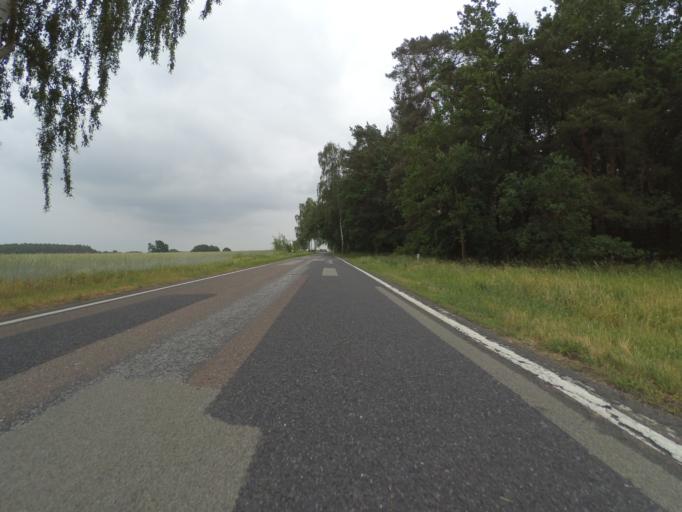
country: DE
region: Mecklenburg-Vorpommern
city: Siggelkow
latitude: 53.3748
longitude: 11.9912
